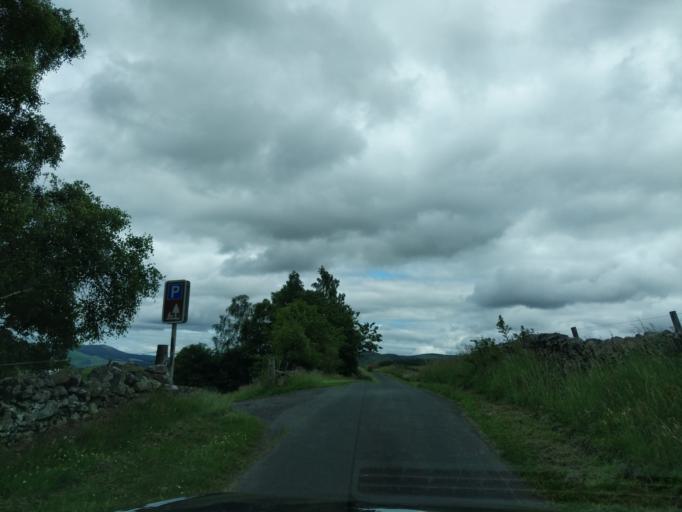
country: GB
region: Scotland
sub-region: The Scottish Borders
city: Peebles
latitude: 55.6452
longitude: -3.2143
